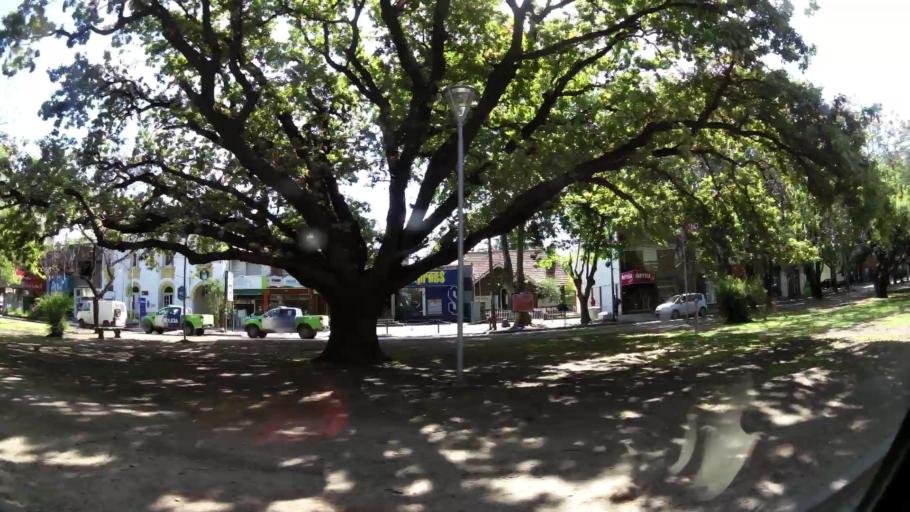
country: AR
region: Buenos Aires
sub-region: Partido de Quilmes
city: Quilmes
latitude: -34.8064
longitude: -58.2781
